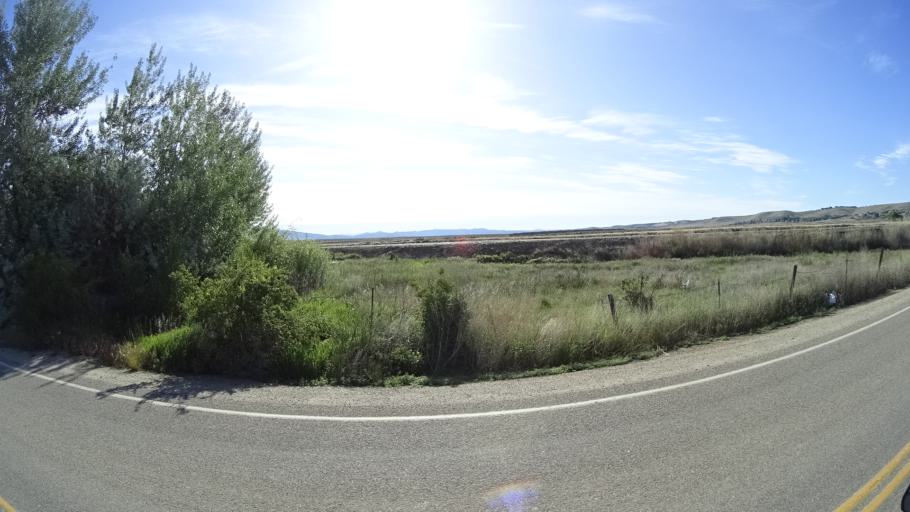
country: US
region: Idaho
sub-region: Ada County
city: Garden City
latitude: 43.5353
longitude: -116.2808
